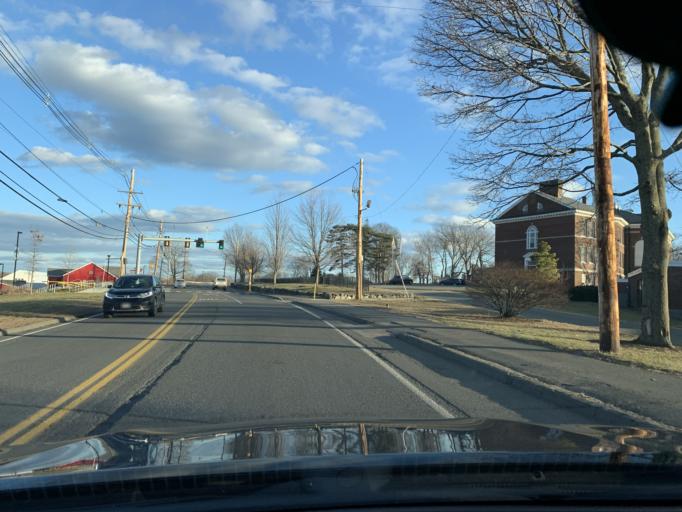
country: US
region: Massachusetts
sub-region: Essex County
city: Middleton
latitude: 42.5911
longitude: -70.9787
